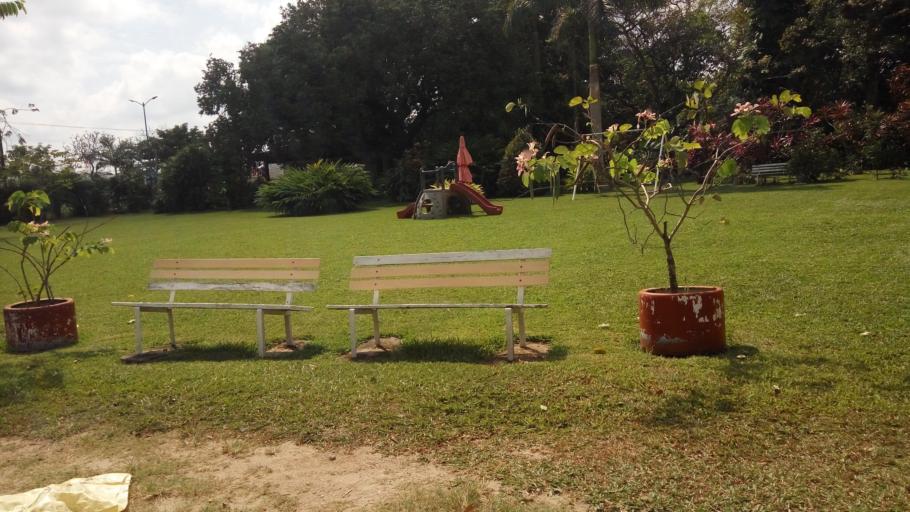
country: MX
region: Tabasco
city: Comalcalco
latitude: 18.2655
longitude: -93.2280
